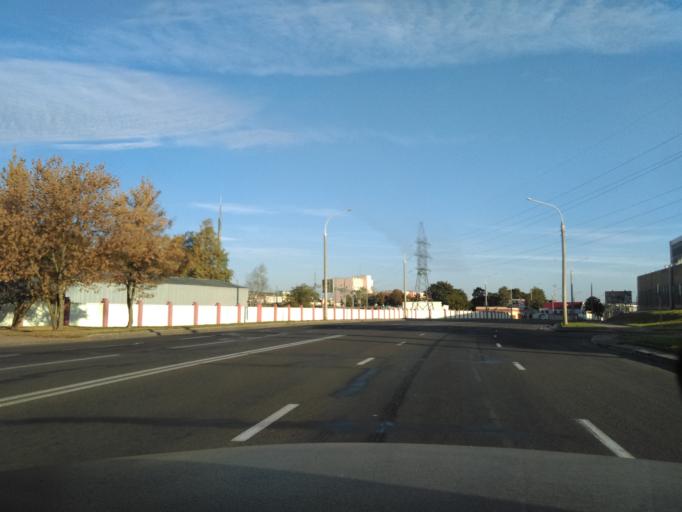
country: BY
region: Minsk
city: Minsk
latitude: 53.8828
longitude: 27.5797
